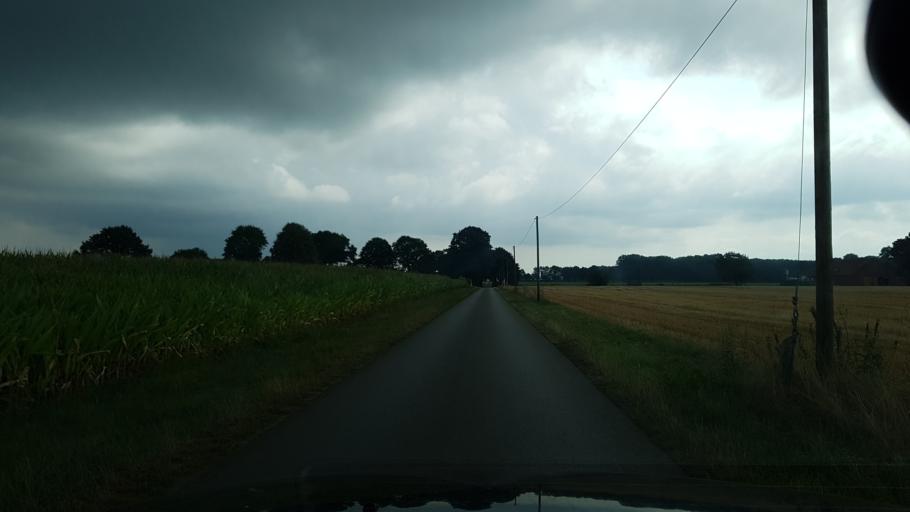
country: DE
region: Lower Saxony
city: Varrel
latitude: 52.6741
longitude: 8.7201
